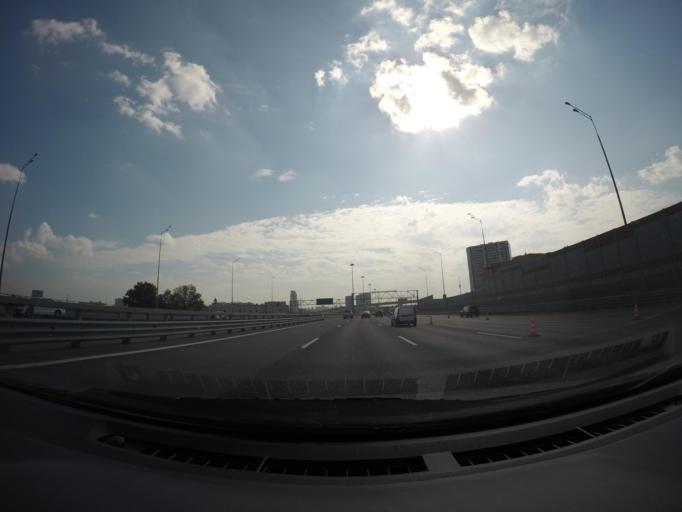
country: RU
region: Moskovskaya
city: Levoberezhnaya
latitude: 55.8917
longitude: 37.4850
